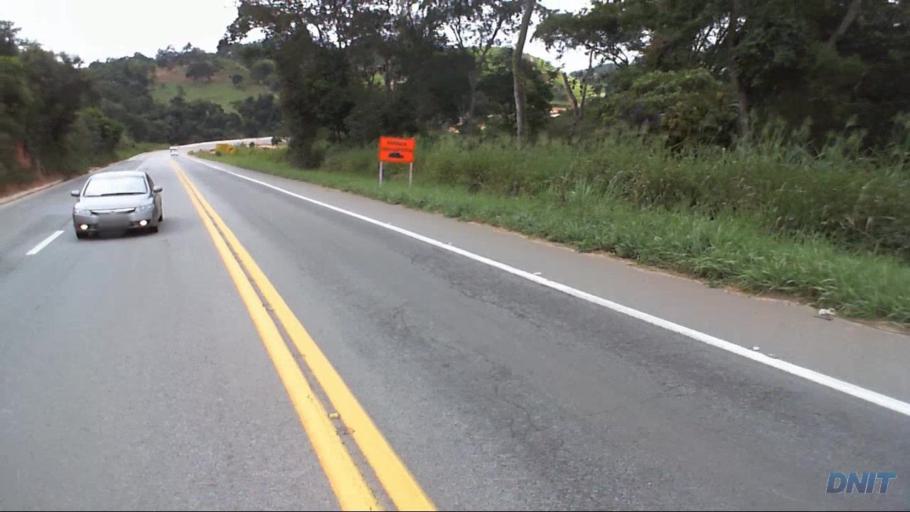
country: BR
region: Minas Gerais
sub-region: Caete
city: Caete
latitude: -19.7496
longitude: -43.6255
